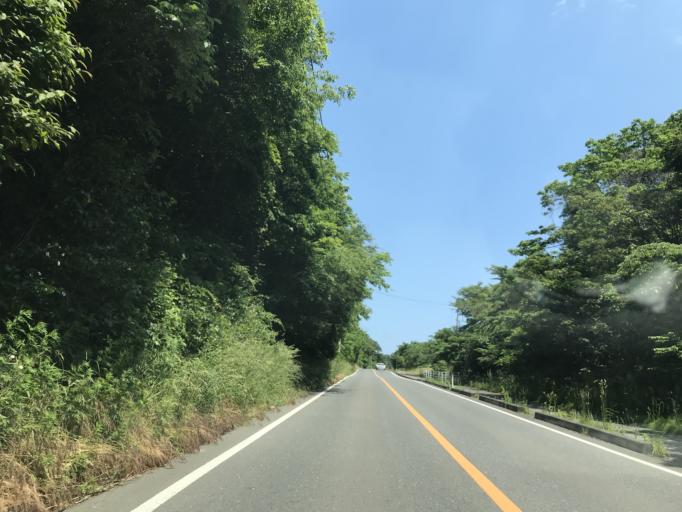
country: JP
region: Miyagi
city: Matsushima
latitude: 38.3785
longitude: 141.1327
